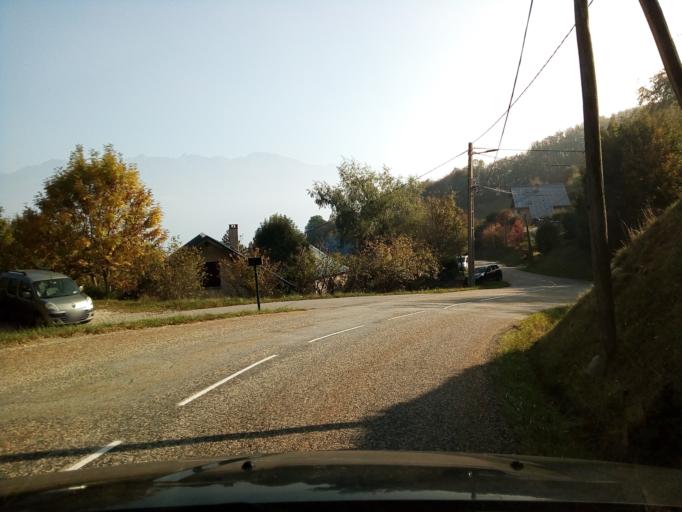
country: FR
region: Rhone-Alpes
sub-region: Departement de l'Isere
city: Bernin
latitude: 45.2893
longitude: 5.8478
